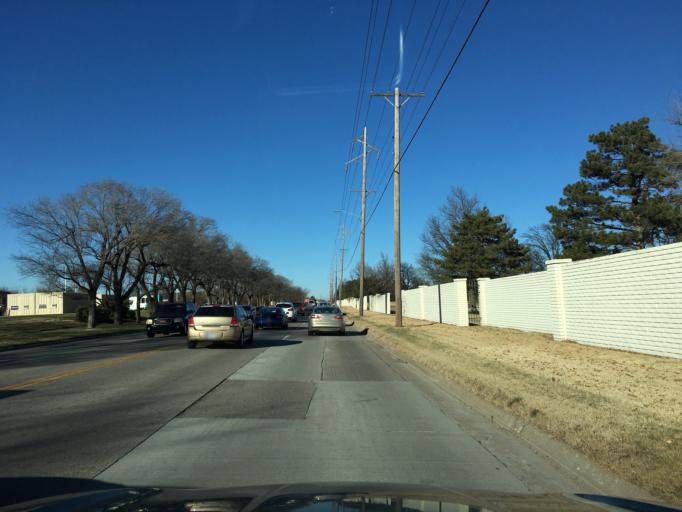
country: US
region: Kansas
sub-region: Sedgwick County
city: Bellaire
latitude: 37.7026
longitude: -97.2446
